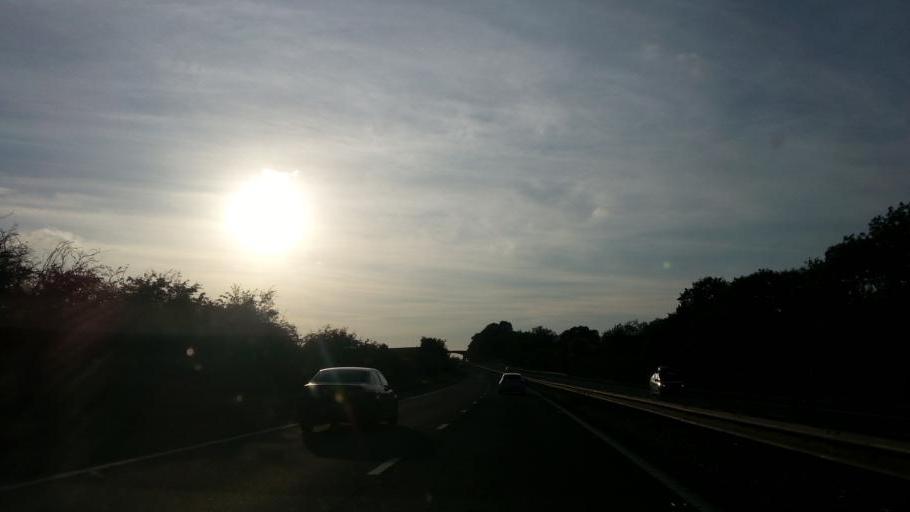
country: GB
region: England
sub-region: Herefordshire
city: Ross on Wye
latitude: 51.9292
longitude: -2.5387
